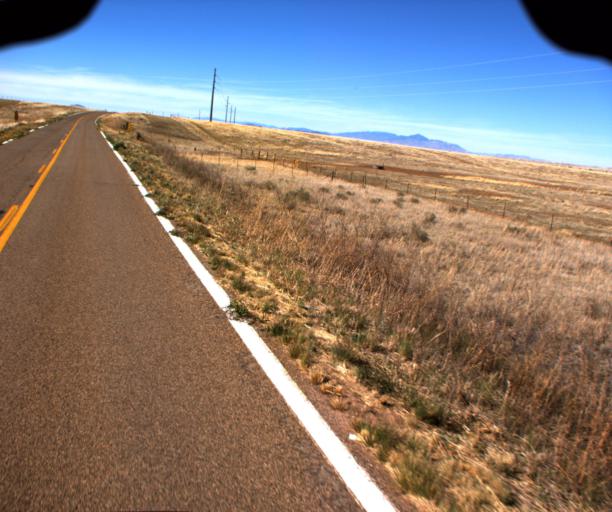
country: US
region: Arizona
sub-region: Cochise County
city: Huachuca City
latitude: 31.6404
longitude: -110.5998
